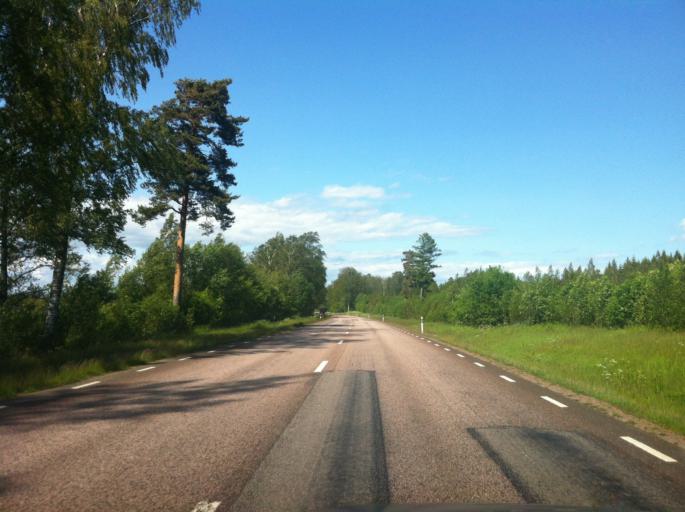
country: SE
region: Vaestra Goetaland
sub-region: Gullspangs Kommun
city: Gullspang
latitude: 59.0618
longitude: 14.1501
